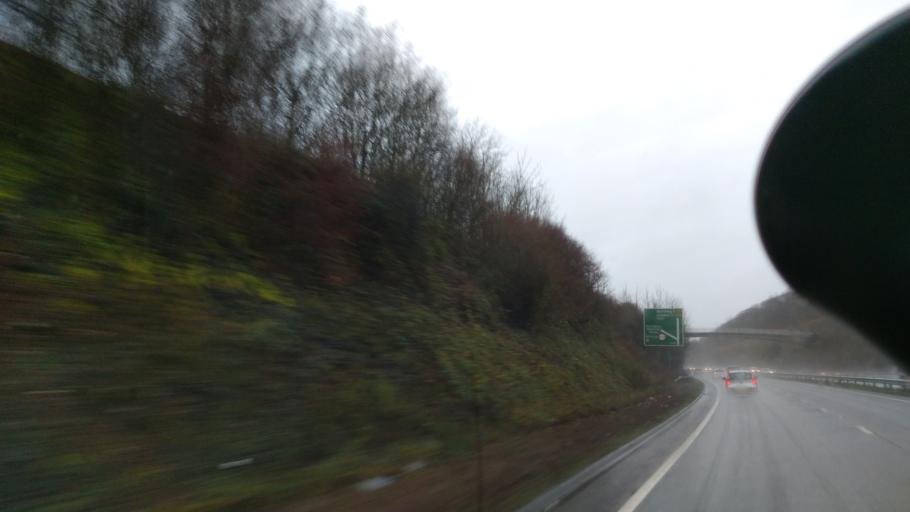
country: GB
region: England
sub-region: Brighton and Hove
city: Brighton
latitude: 50.8647
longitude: -0.1067
